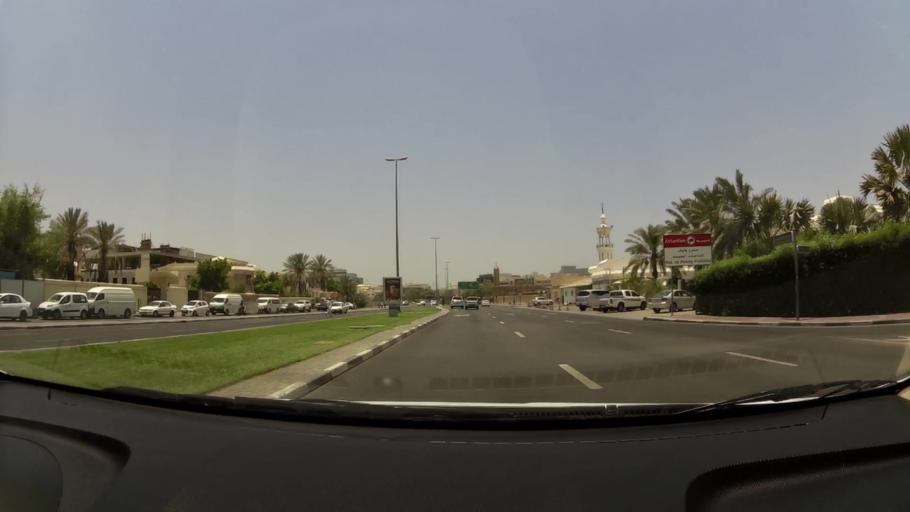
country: AE
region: Ash Shariqah
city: Sharjah
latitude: 25.2774
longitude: 55.3192
